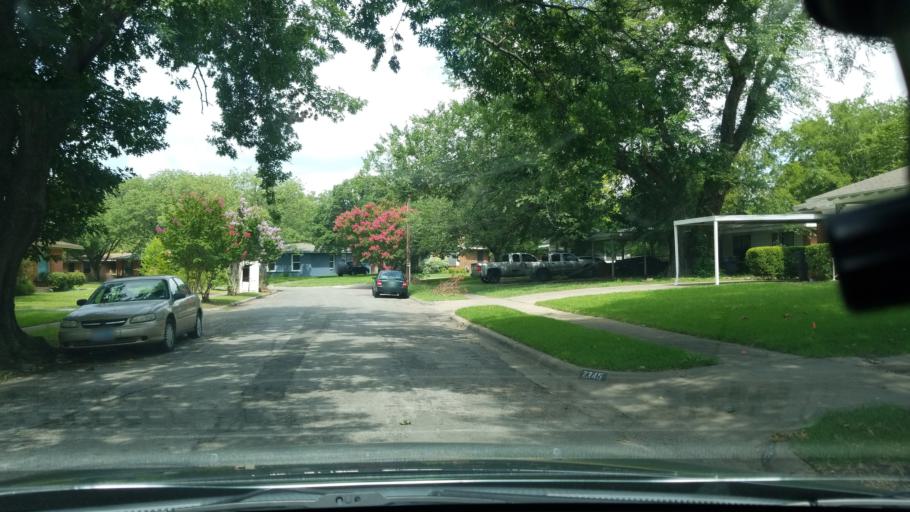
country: US
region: Texas
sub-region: Dallas County
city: Garland
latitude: 32.8316
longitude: -96.6762
